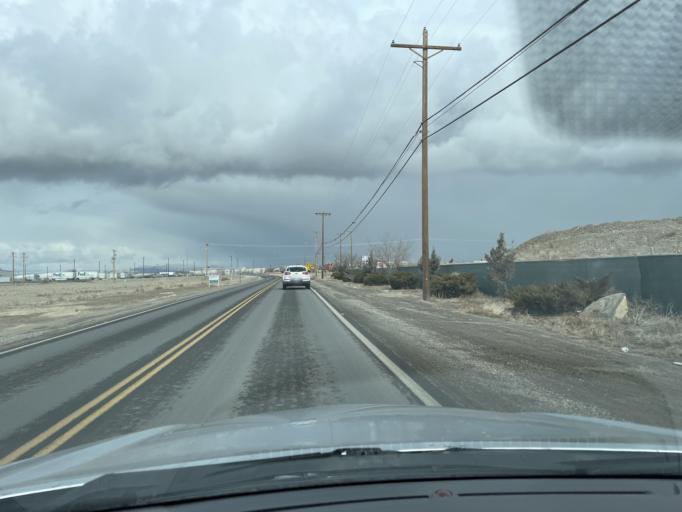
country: US
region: Colorado
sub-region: Mesa County
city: Redlands
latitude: 39.1045
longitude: -108.6267
